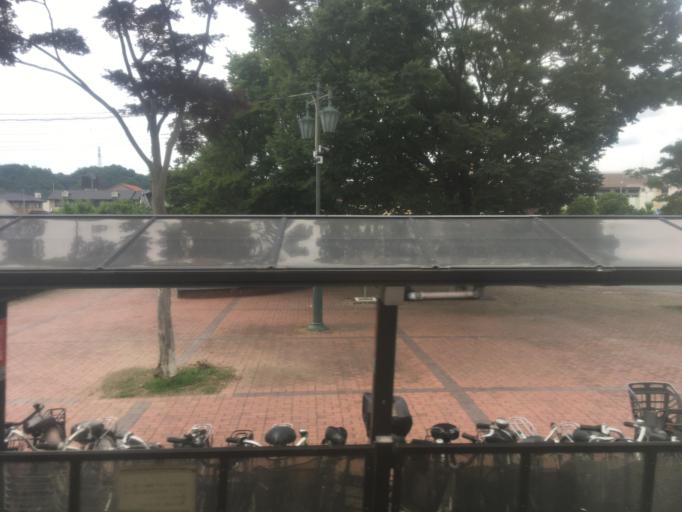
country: JP
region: Gunma
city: Tomioka
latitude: 36.2608
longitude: 138.9023
